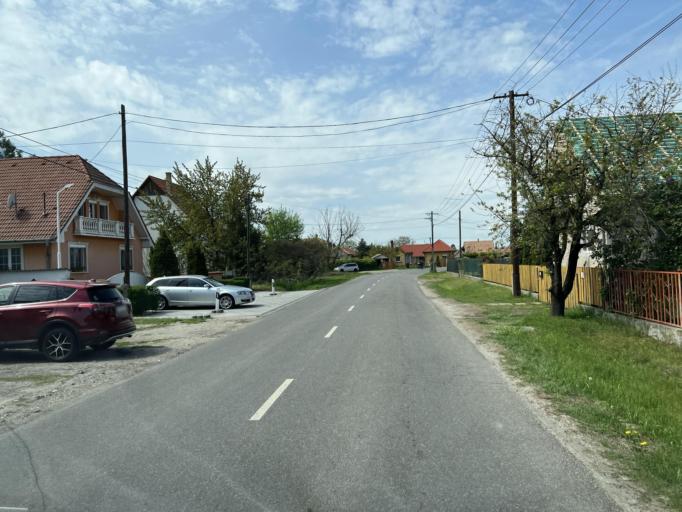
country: HU
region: Pest
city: Albertirsa
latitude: 47.2296
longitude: 19.6127
